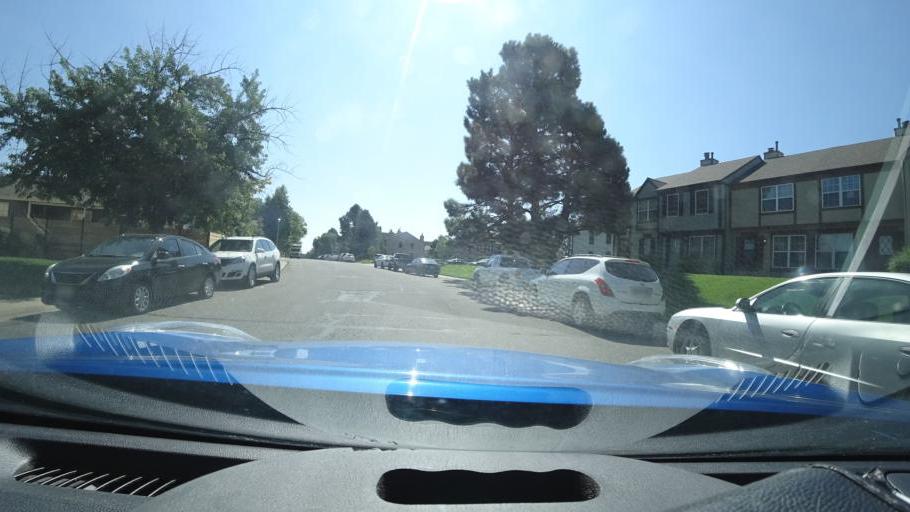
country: US
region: Colorado
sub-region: Adams County
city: Aurora
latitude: 39.6870
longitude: -104.8231
